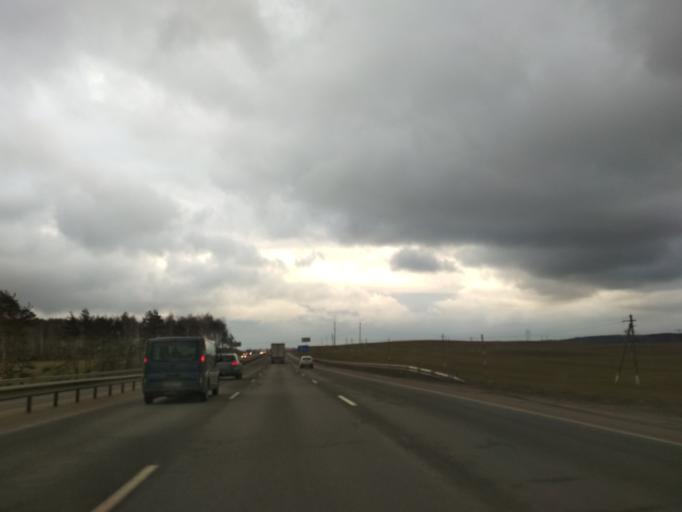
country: BY
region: Minsk
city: Pryvol'ny
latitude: 53.8172
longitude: 27.7686
